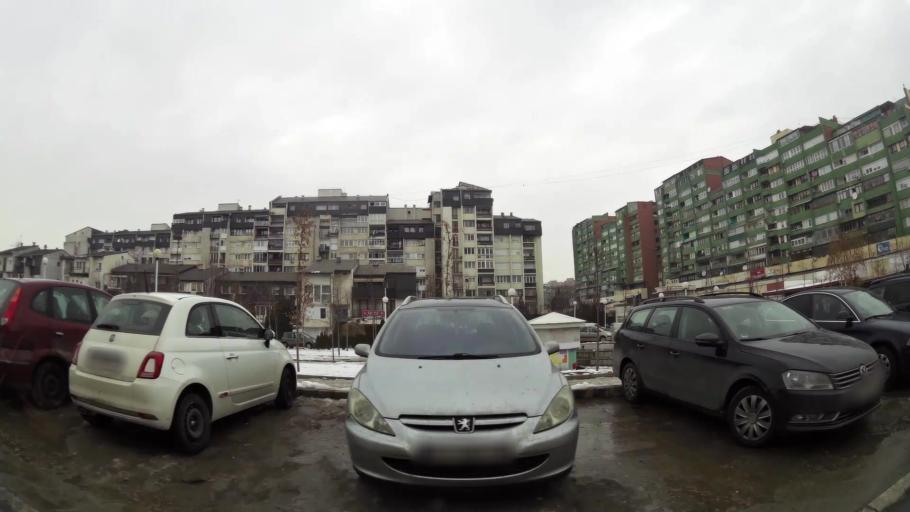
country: XK
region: Pristina
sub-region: Komuna e Prishtines
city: Pristina
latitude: 42.6514
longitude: 21.1559
